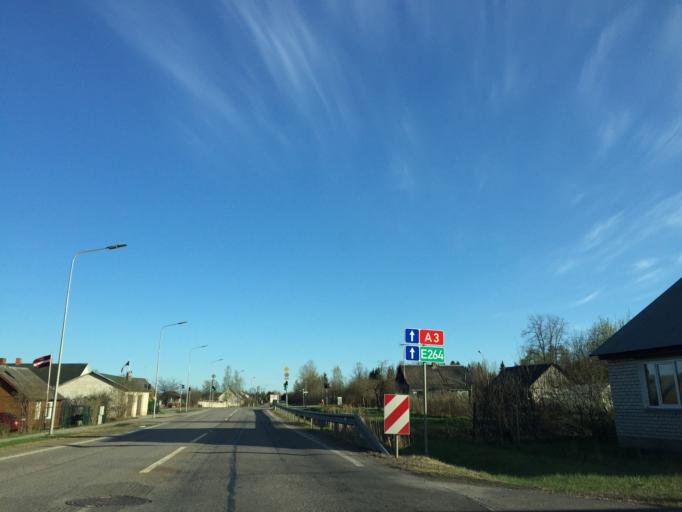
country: LV
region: Valkas Rajons
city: Valka
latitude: 57.7711
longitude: 25.9988
